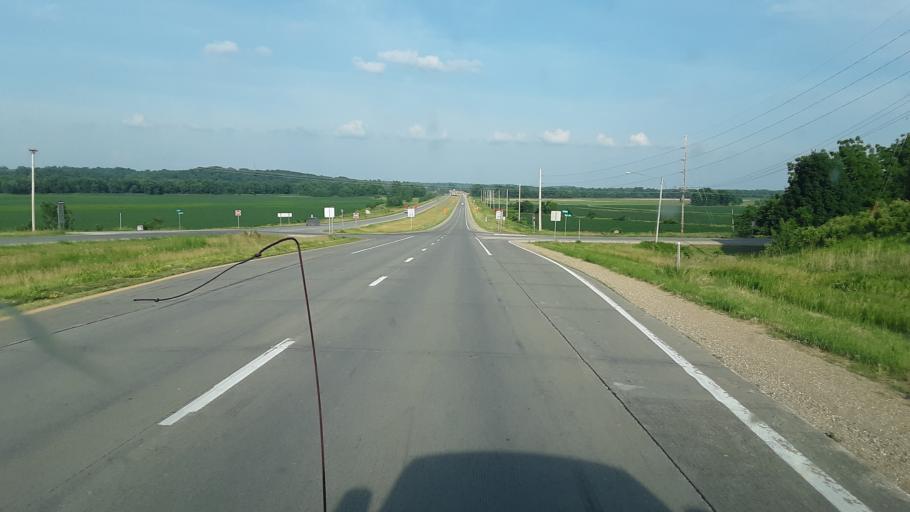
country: US
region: Iowa
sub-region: Tama County
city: Toledo
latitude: 42.0051
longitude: -92.7310
